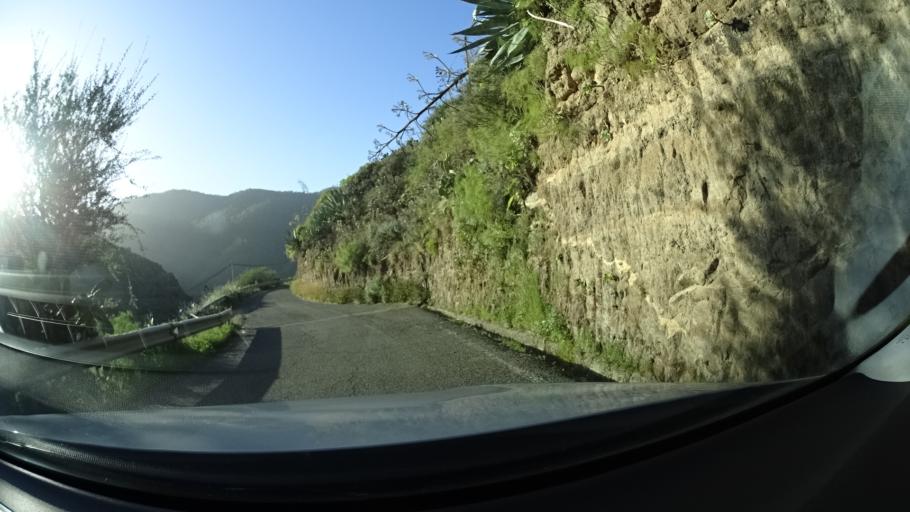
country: ES
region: Canary Islands
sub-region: Provincia de Las Palmas
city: Artenara
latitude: 28.0459
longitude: -15.6638
